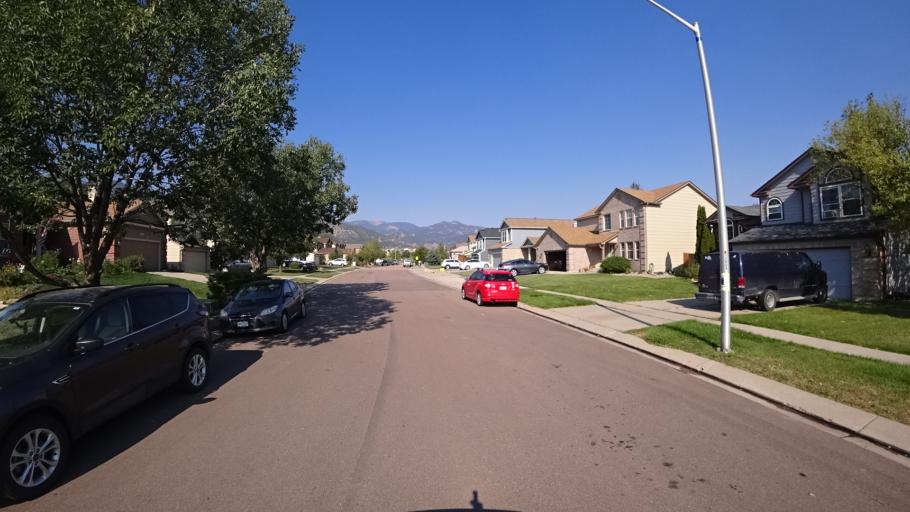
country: US
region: Colorado
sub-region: El Paso County
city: Stratmoor
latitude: 38.7713
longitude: -104.8028
